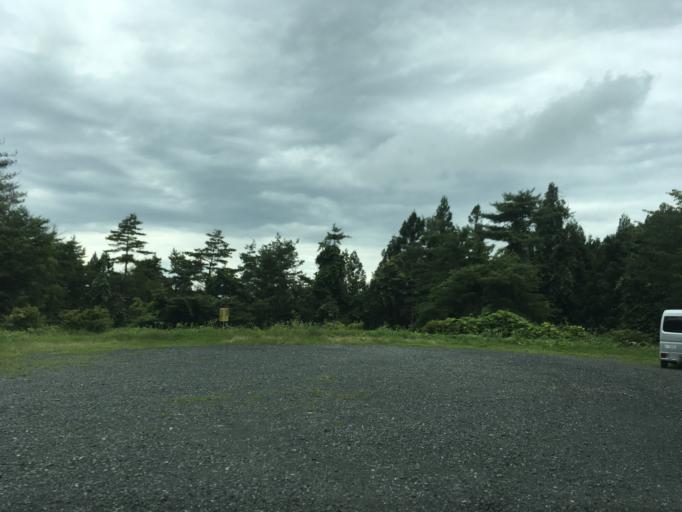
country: JP
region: Iwate
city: Ichinoseki
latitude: 38.8683
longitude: 141.3994
